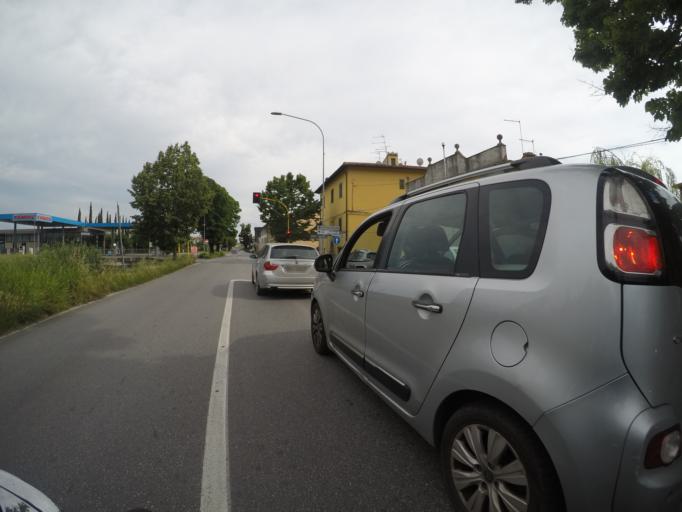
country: IT
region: Tuscany
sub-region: Province of Pisa
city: Madonna dell'Acqua
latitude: 43.7293
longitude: 10.3883
